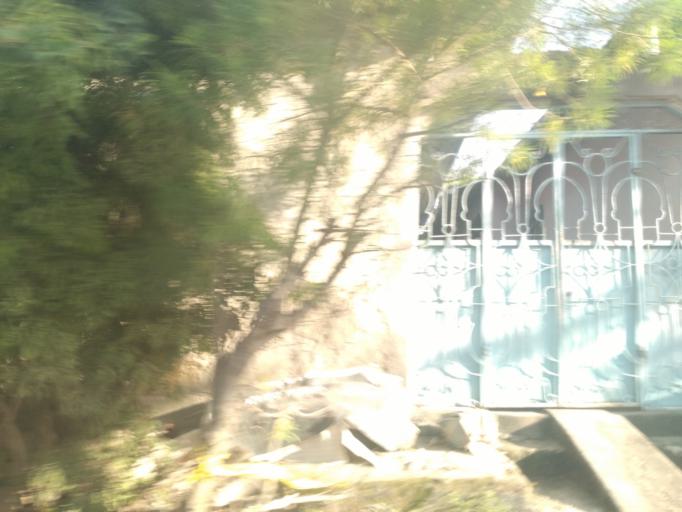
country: TZ
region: Zanzibar Urban/West
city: Zanzibar
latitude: -6.1695
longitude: 39.1964
